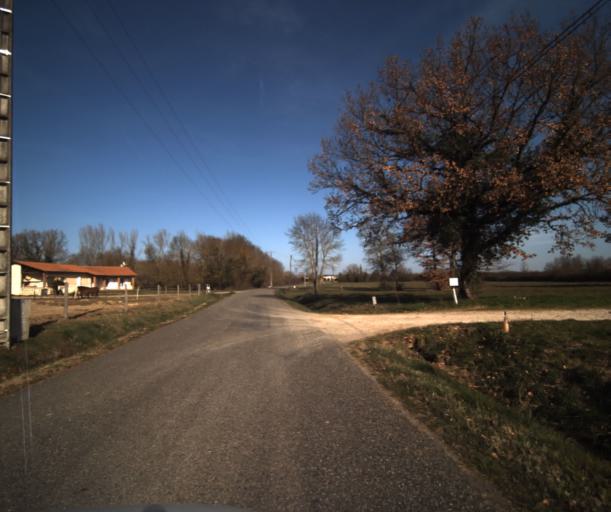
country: FR
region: Midi-Pyrenees
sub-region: Departement du Tarn-et-Garonne
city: Campsas
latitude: 43.9255
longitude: 1.3216
